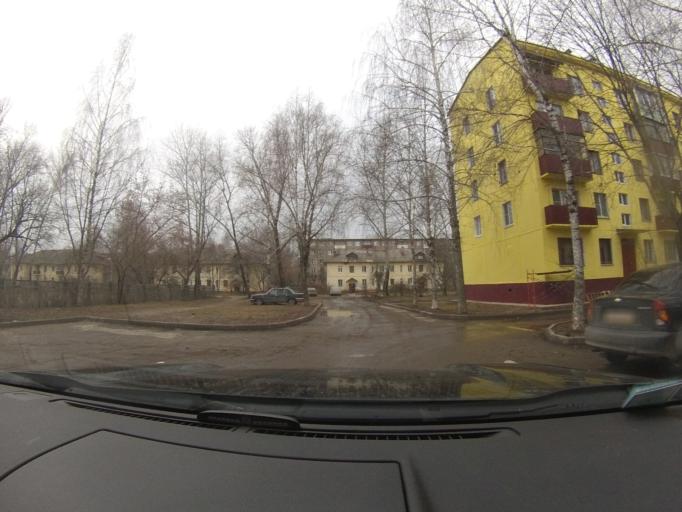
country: RU
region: Moskovskaya
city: Peski
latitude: 55.2491
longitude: 38.7609
